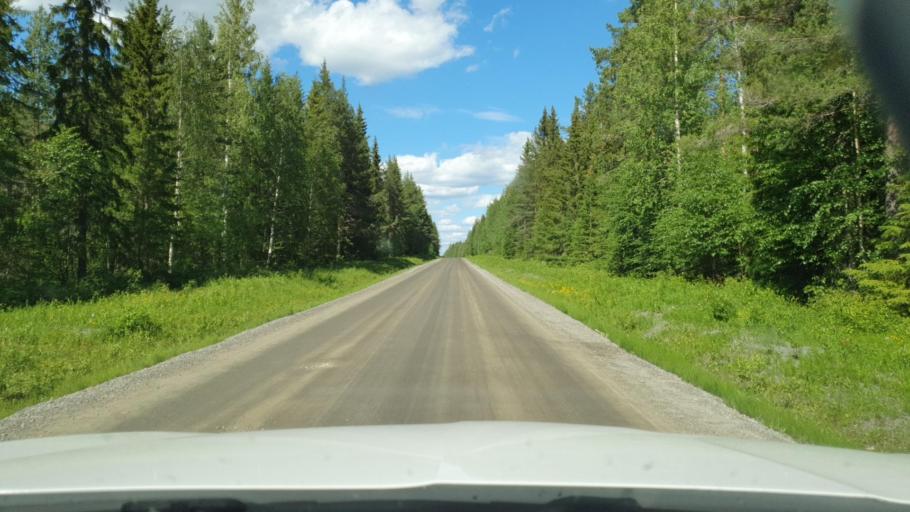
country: SE
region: Vaesterbotten
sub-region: Skelleftea Kommun
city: Forsbacka
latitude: 64.7714
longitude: 20.5172
